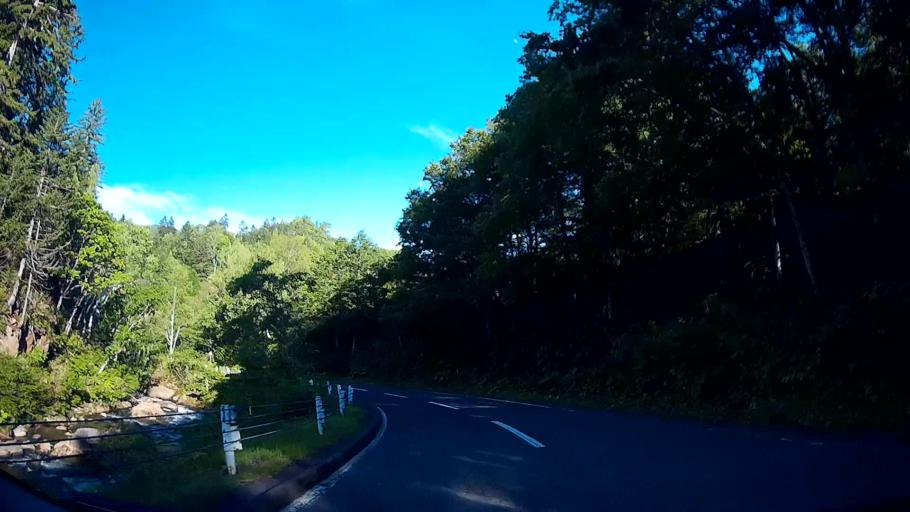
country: JP
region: Hokkaido
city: Otaru
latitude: 42.9863
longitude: 141.0669
